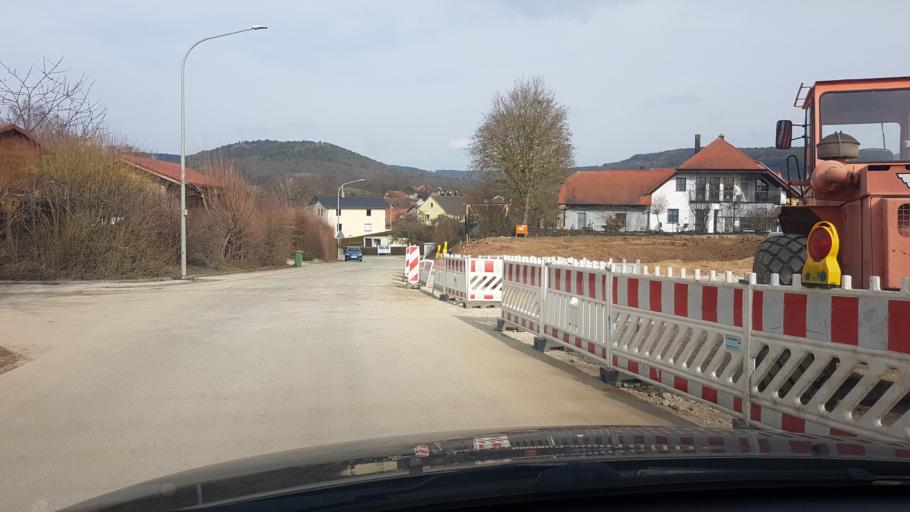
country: DE
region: Bavaria
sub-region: Upper Franconia
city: Ebensfeld
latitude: 50.0338
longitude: 10.9978
